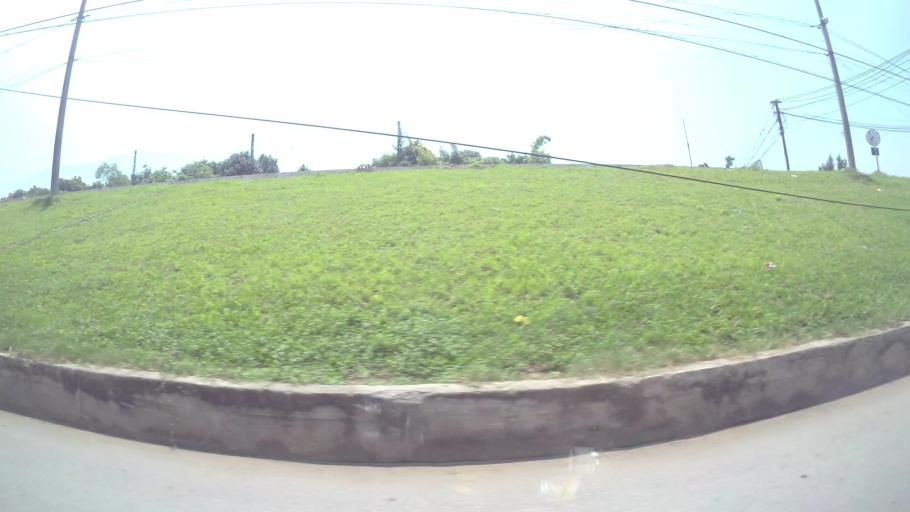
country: VN
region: Ha Noi
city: Hoan Kiem
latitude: 21.0224
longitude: 105.8905
